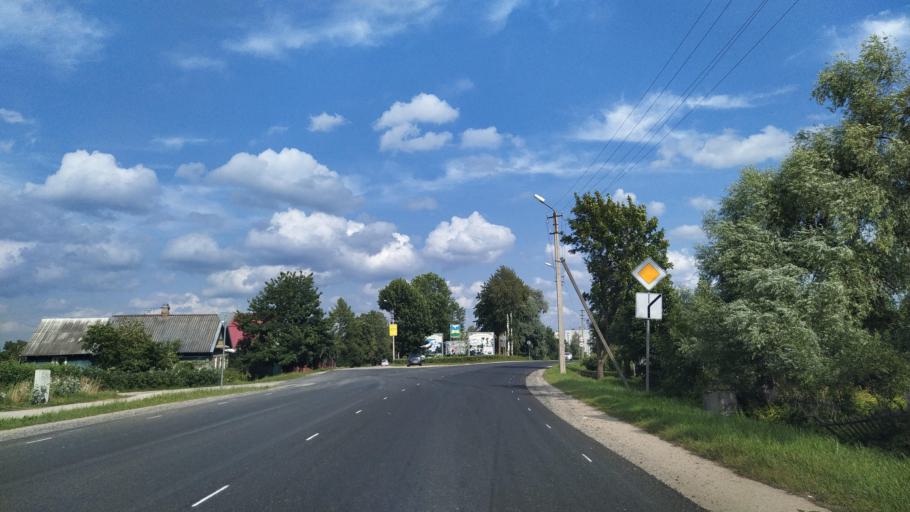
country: RU
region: Pskov
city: Porkhov
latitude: 57.7604
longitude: 29.5451
